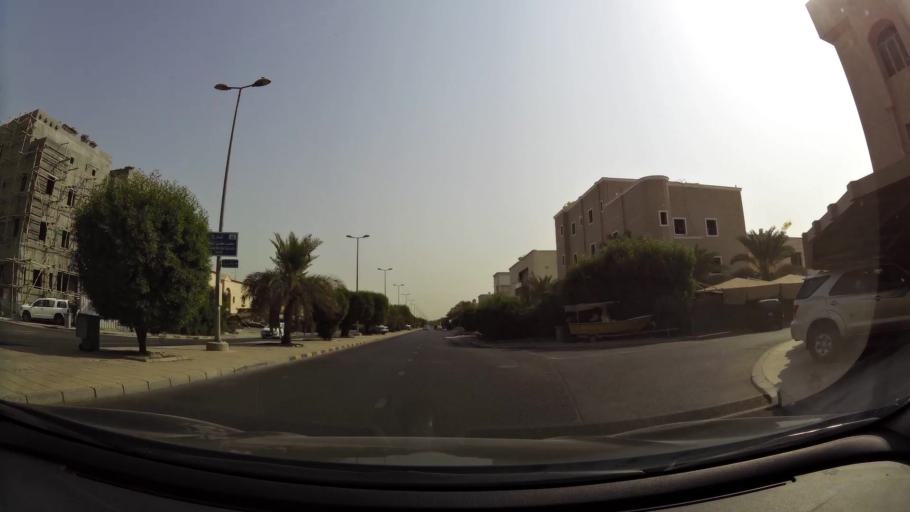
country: KW
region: Al Asimah
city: Ar Rabiyah
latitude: 29.2911
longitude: 47.8842
